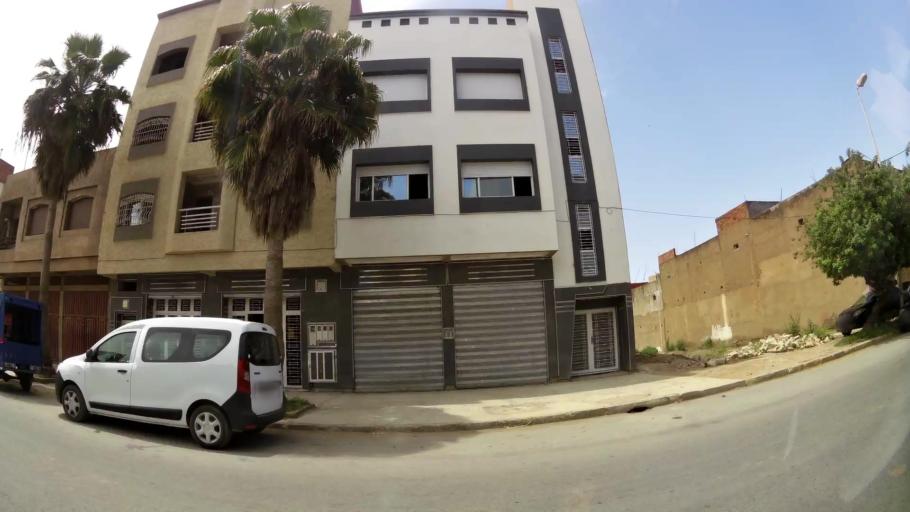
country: MA
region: Rabat-Sale-Zemmour-Zaer
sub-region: Khemisset
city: Khemisset
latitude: 33.8247
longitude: -6.0772
